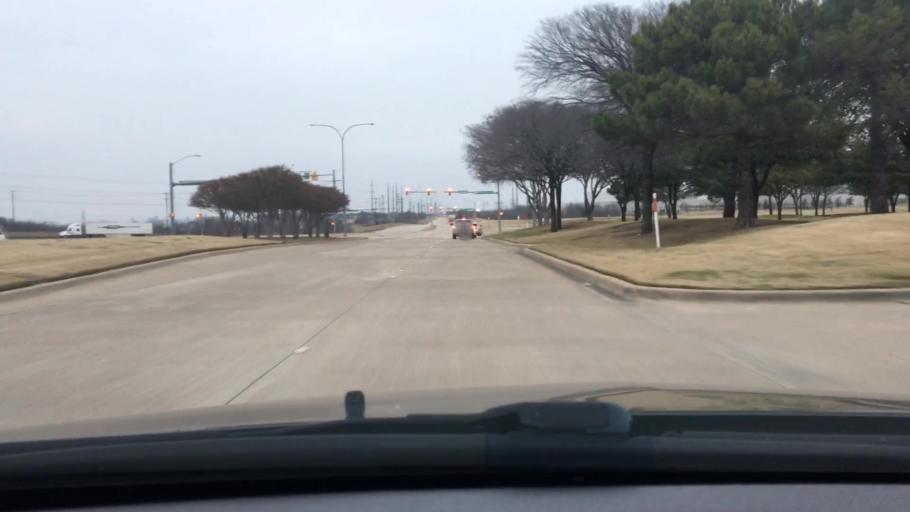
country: US
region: Texas
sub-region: Tarrant County
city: Keller
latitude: 32.9776
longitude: -97.2627
